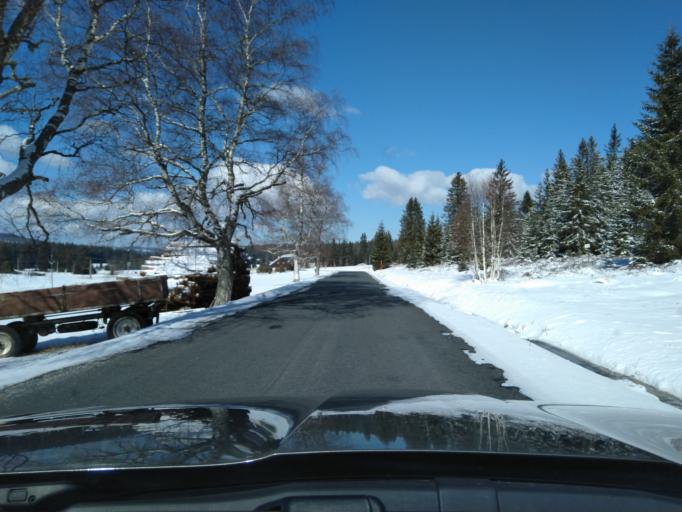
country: CZ
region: Plzensky
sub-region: Okres Klatovy
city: Kasperske Hory
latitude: 49.0498
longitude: 13.5755
